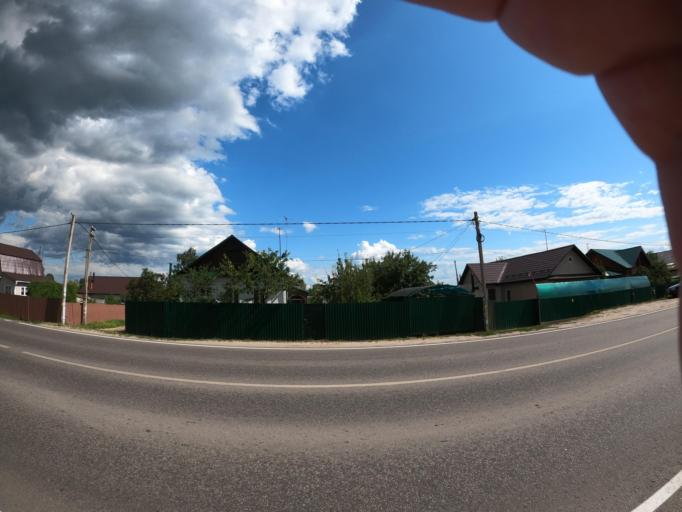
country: RU
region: Moskovskaya
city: Konobeyevo
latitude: 55.4088
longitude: 38.6613
